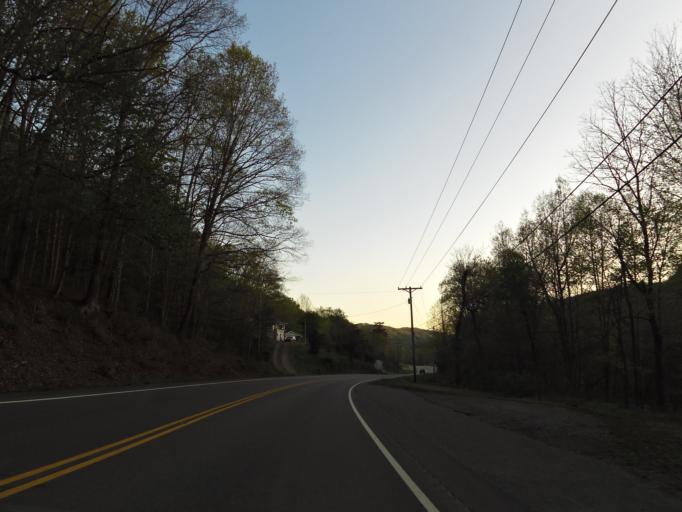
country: US
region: Tennessee
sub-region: Campbell County
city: Fincastle
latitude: 36.4313
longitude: -84.0811
